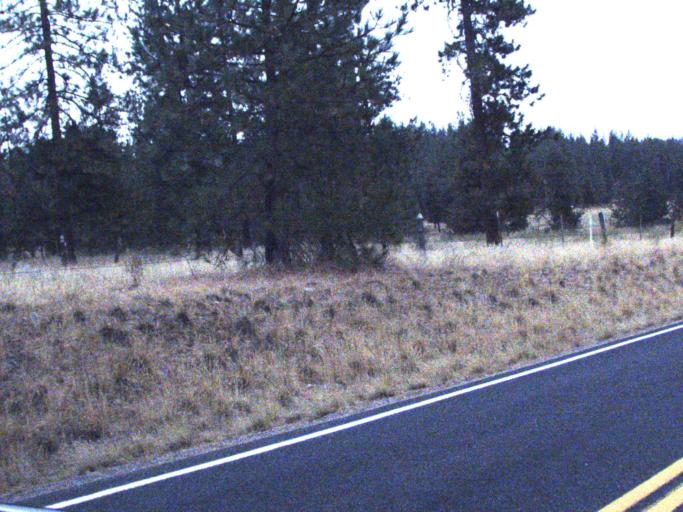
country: US
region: Washington
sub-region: Spokane County
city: Fairchild Air Force Base
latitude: 47.8754
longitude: -117.8378
